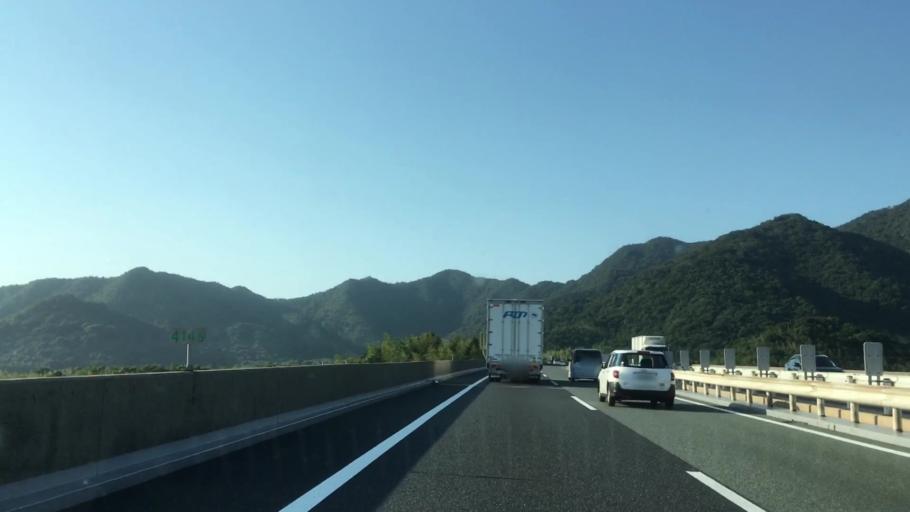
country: JP
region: Yamaguchi
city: Ogori-shimogo
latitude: 34.0945
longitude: 131.4547
